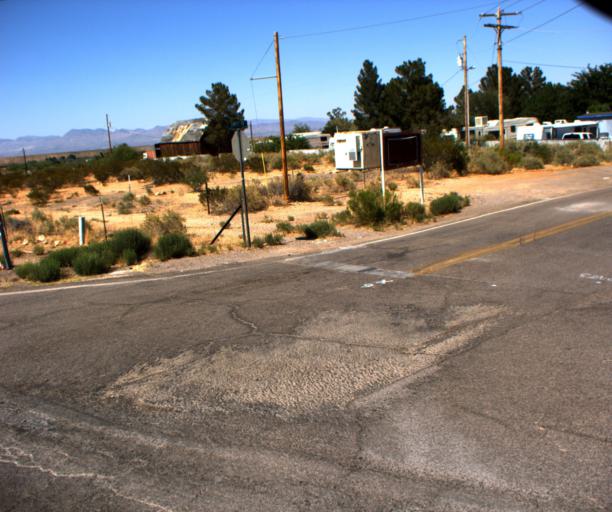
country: US
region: Arizona
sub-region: Graham County
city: Swift Trail Junction
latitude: 32.7298
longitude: -109.7143
